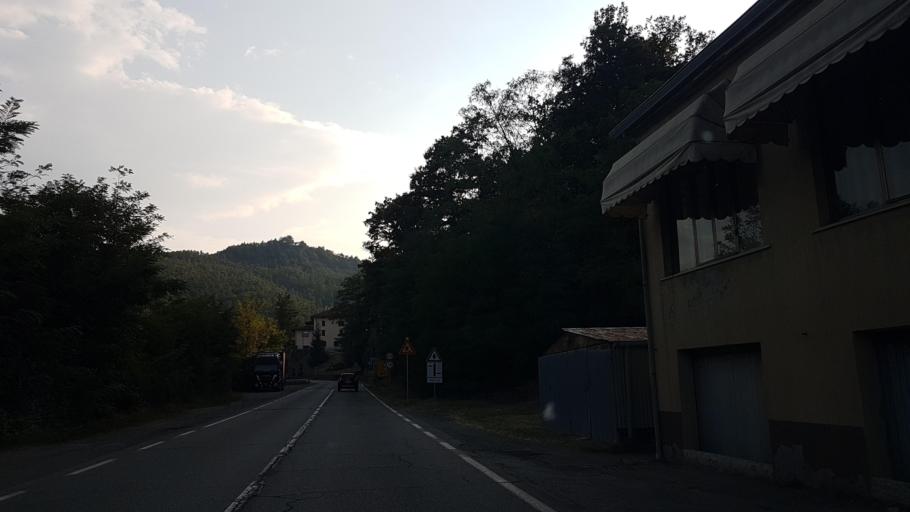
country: IT
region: Emilia-Romagna
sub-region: Provincia di Parma
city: Stazione Valmozzola
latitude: 44.5854
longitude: 9.9439
